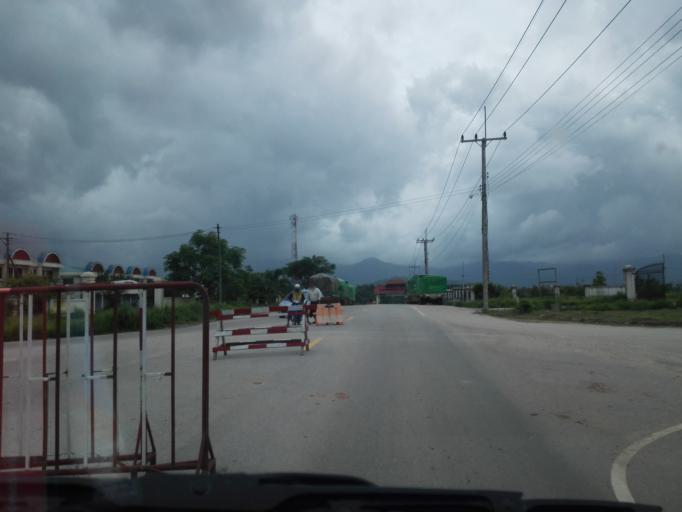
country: TH
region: Tak
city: Mae Sot
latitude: 16.6951
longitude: 98.4228
